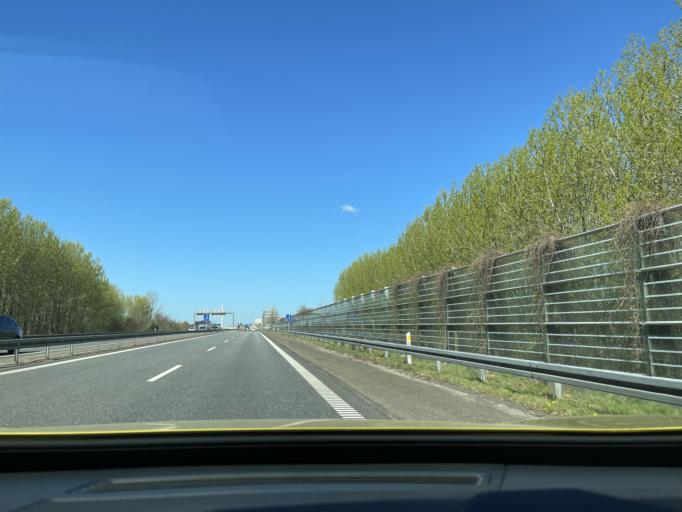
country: DK
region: Central Jutland
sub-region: Herning Kommune
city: Herning
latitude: 56.1290
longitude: 9.0006
